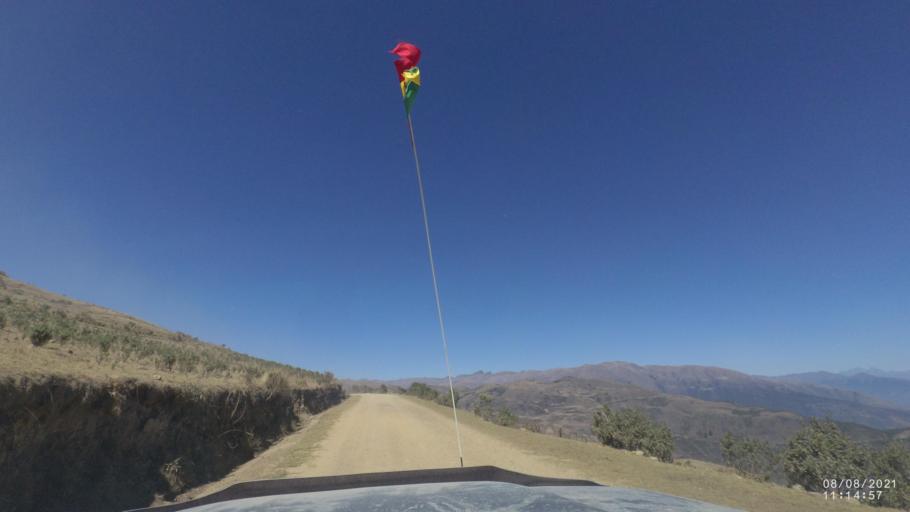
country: BO
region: Cochabamba
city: Colchani
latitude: -16.7727
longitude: -66.6673
